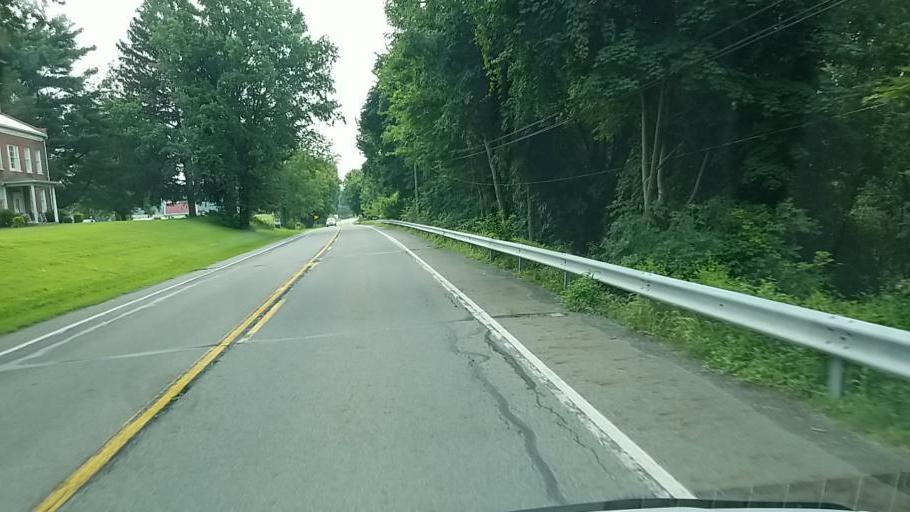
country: US
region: Pennsylvania
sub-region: Dauphin County
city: Millersburg
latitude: 40.5038
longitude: -76.9522
